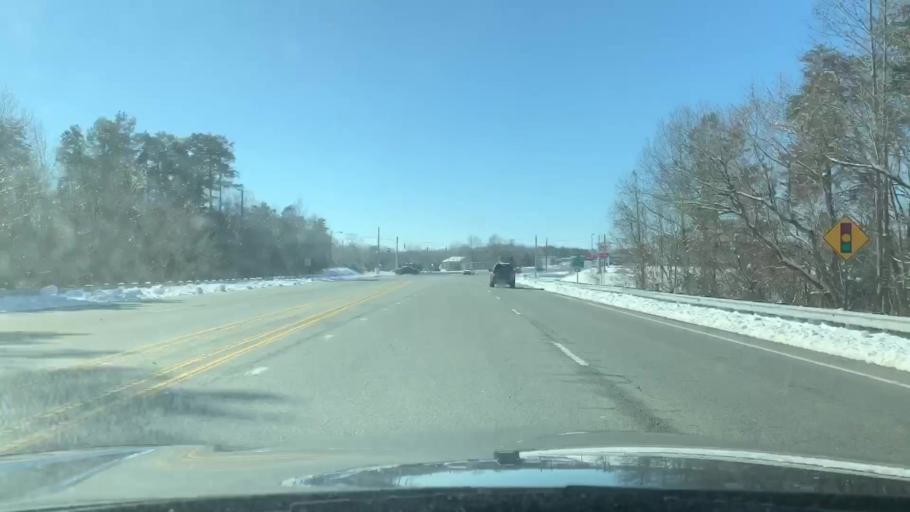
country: US
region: North Carolina
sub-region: Alamance County
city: Haw River
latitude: 36.0922
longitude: -79.3774
